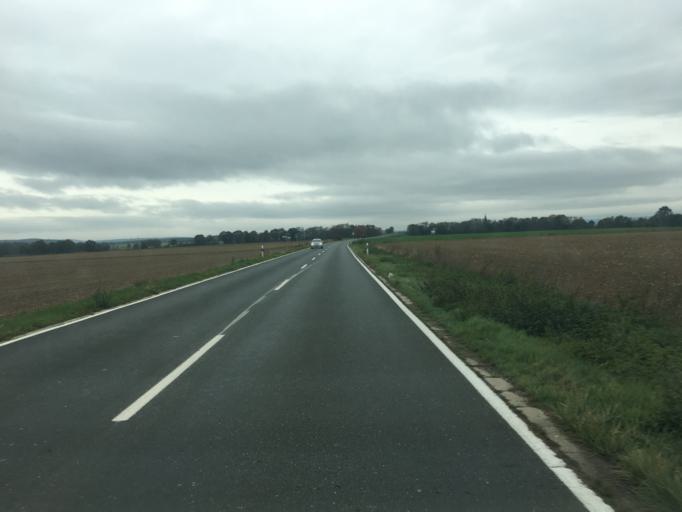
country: DE
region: North Rhine-Westphalia
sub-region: Regierungsbezirk Koln
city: Euskirchen
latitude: 50.6755
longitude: 6.7294
